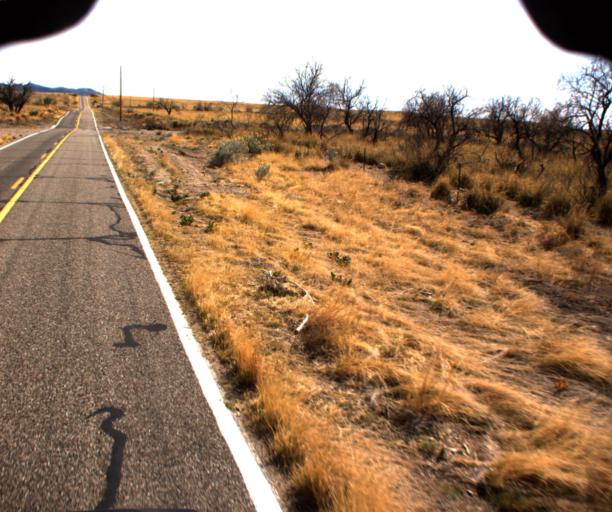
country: US
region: Arizona
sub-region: Cochise County
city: Willcox
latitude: 32.0176
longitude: -109.4401
